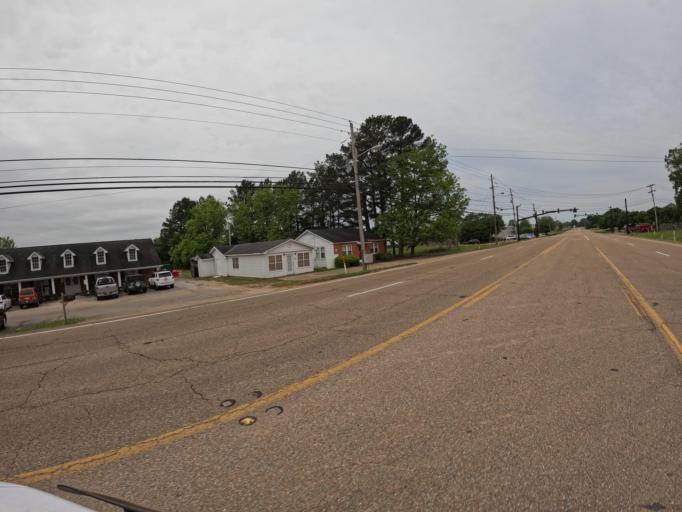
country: US
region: Mississippi
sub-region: Lee County
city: Tupelo
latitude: 34.2948
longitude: -88.7632
